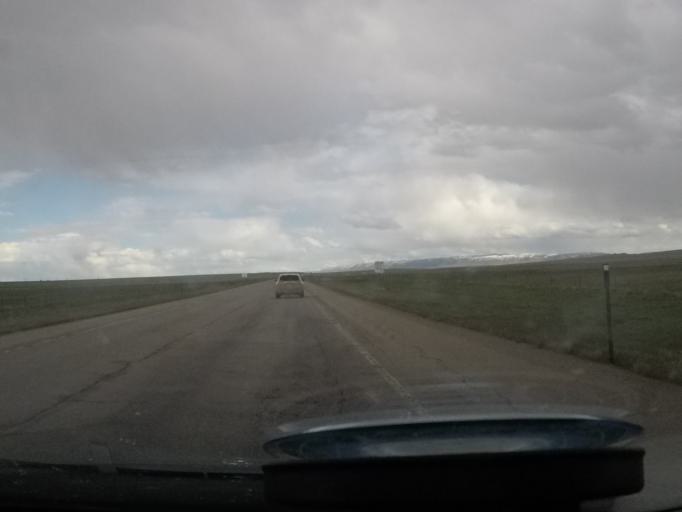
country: US
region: Wyoming
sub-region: Natrona County
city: Mills
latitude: 42.9508
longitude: -106.6346
